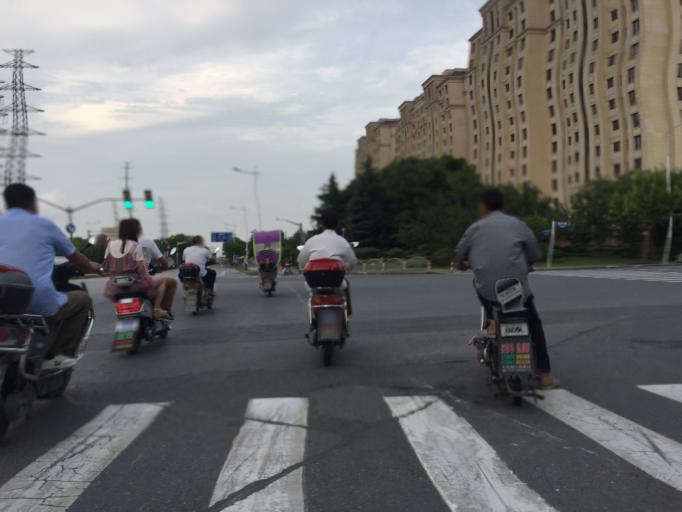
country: CN
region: Shanghai Shi
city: Huamu
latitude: 31.1895
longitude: 121.5413
